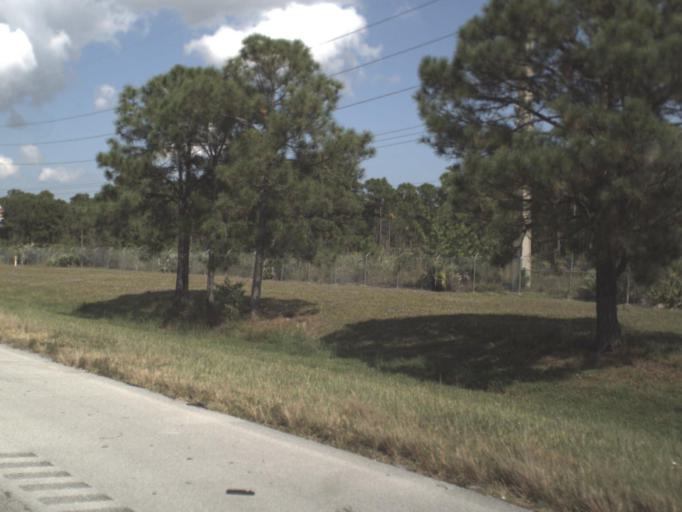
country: US
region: Florida
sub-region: Saint Lucie County
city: Port Saint Lucie
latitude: 27.2541
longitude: -80.3486
